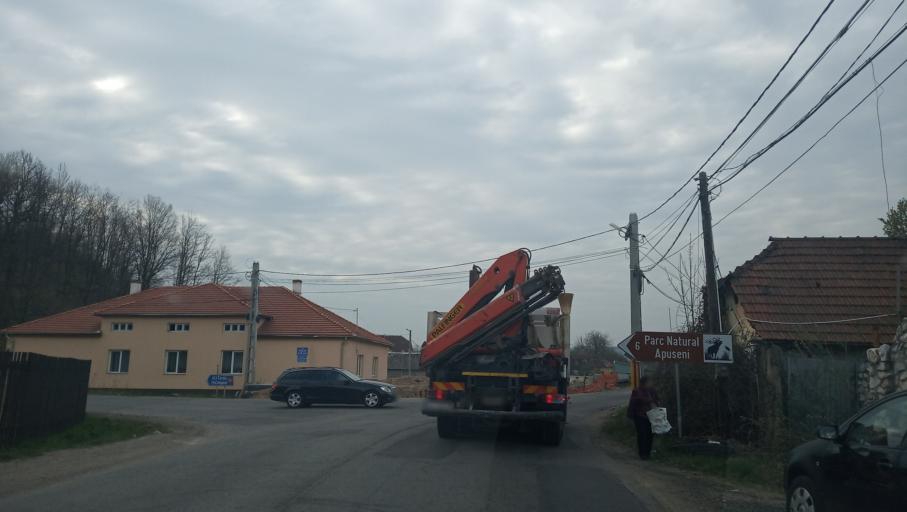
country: RO
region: Bihor
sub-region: Comuna Lunca
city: Lunca
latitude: 46.5239
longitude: 22.4641
